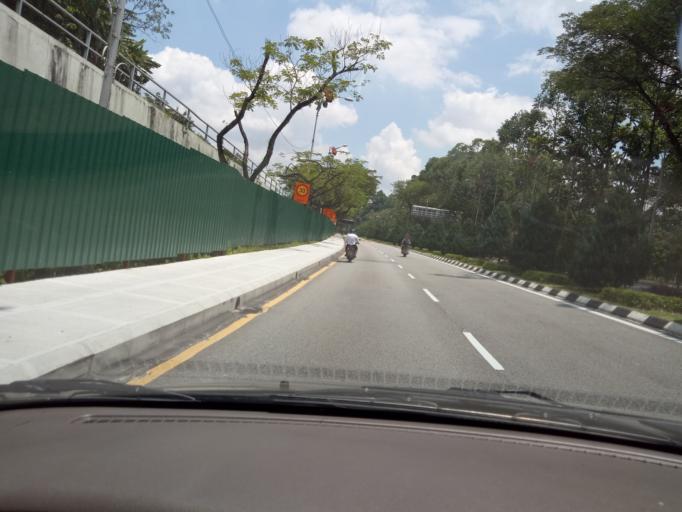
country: MY
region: Kuala Lumpur
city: Kuala Lumpur
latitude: 3.1506
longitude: 101.6894
